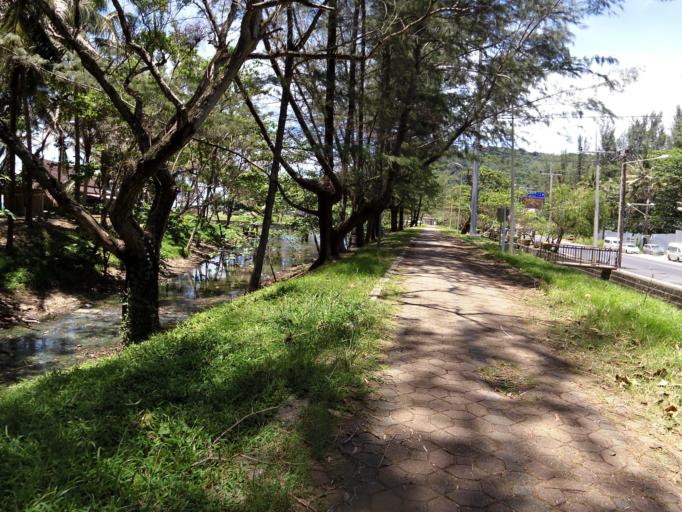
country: TH
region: Phuket
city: Ban Karon
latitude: 7.8535
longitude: 98.2925
